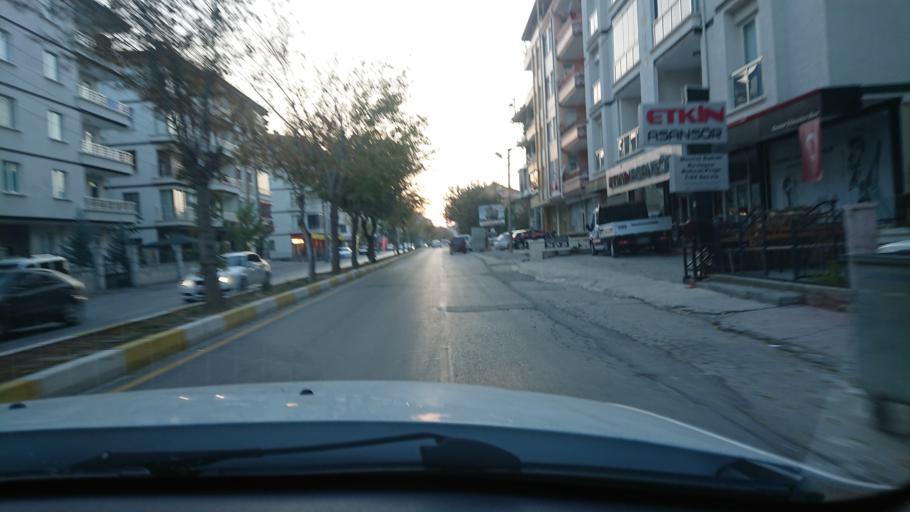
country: TR
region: Aksaray
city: Aksaray
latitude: 38.3623
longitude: 34.0295
